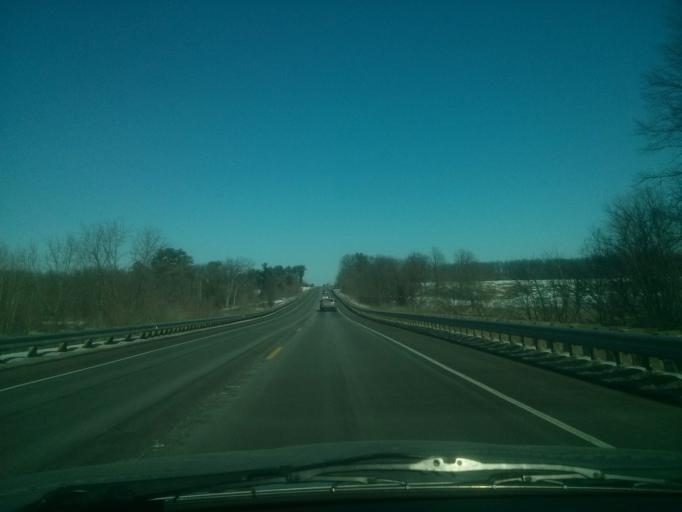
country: US
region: Wisconsin
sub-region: Polk County
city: Clear Lake
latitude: 45.1995
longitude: -92.2837
